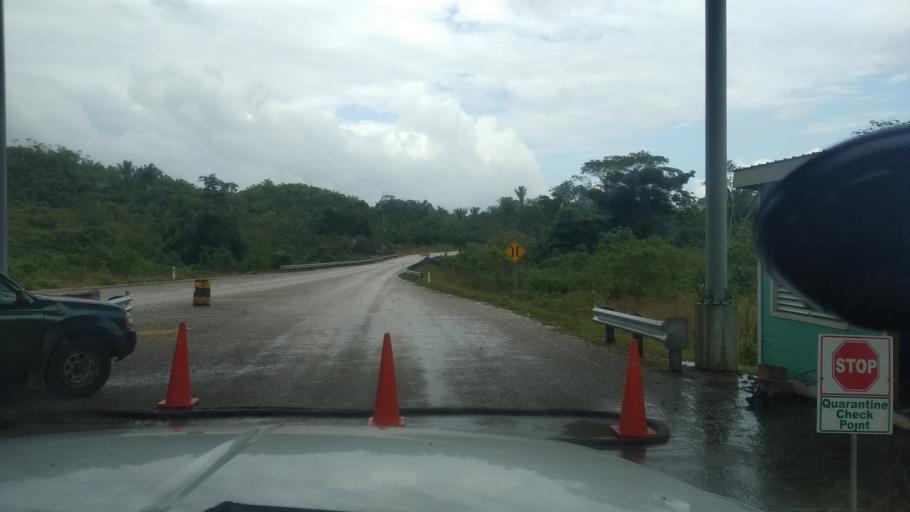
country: GT
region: Peten
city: San Luis
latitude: 16.1895
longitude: -89.1881
